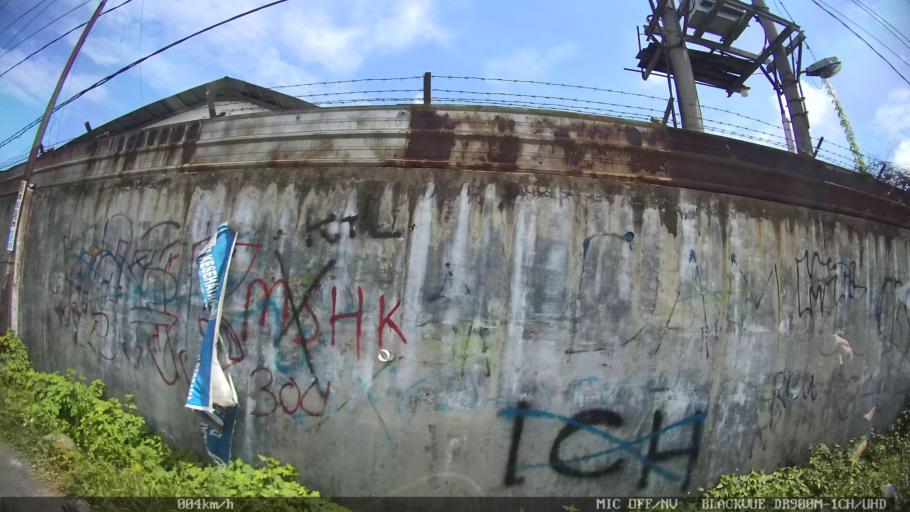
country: ID
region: North Sumatra
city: Medan
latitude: 3.6002
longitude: 98.7477
